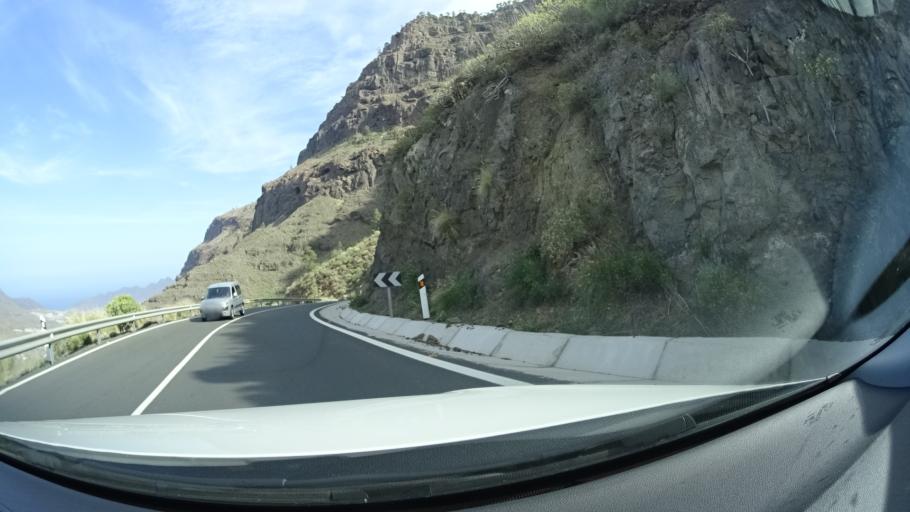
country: ES
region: Canary Islands
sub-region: Provincia de Las Palmas
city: San Nicolas
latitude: 27.9407
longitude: -15.7577
